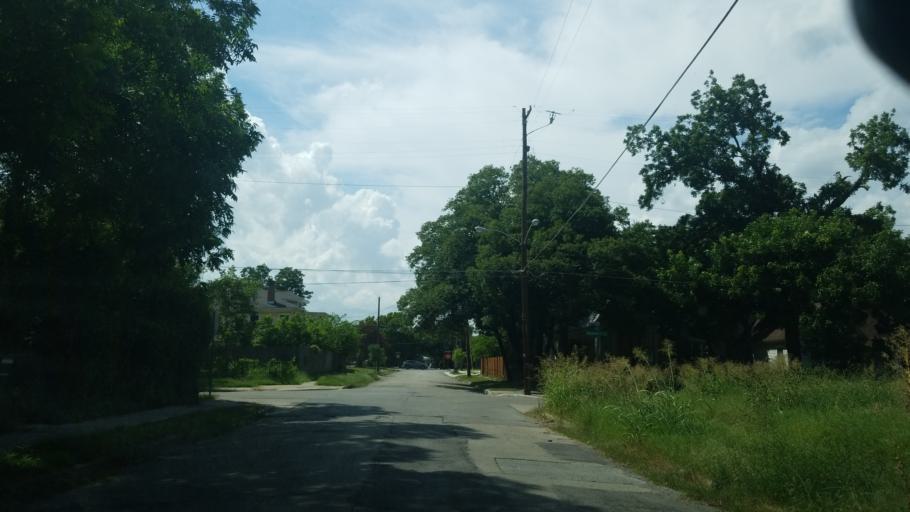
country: US
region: Texas
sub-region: Dallas County
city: Dallas
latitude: 32.7995
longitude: -96.7740
